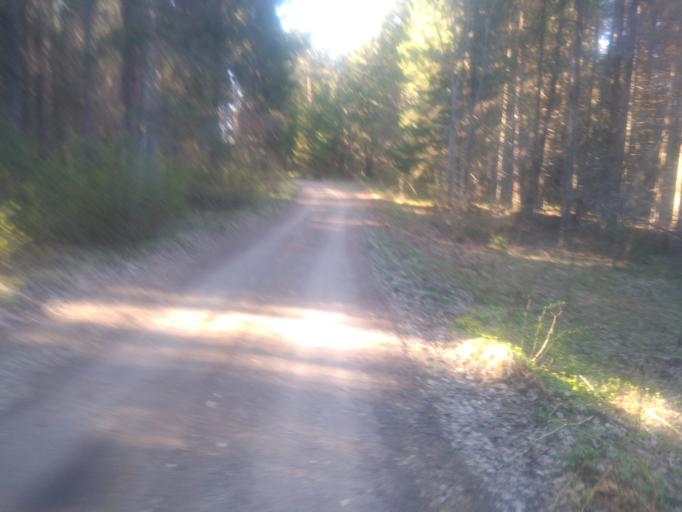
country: LV
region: Vecpiebalga
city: Vecpiebalga
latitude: 57.0082
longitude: 25.8436
